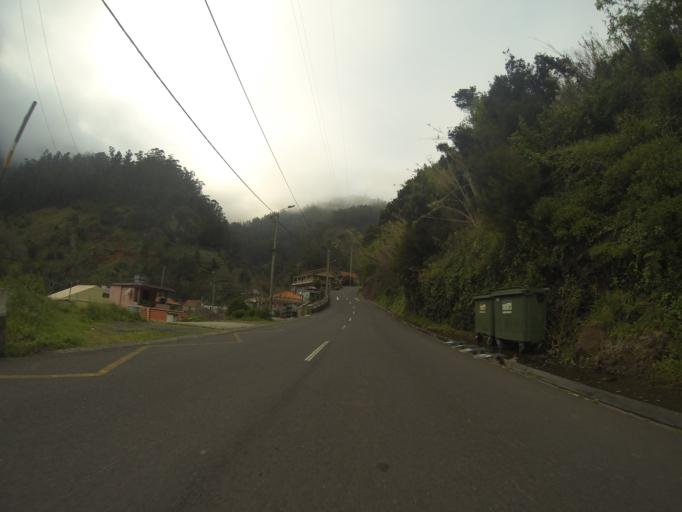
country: PT
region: Madeira
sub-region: Camara de Lobos
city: Curral das Freiras
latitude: 32.7438
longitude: -16.9650
